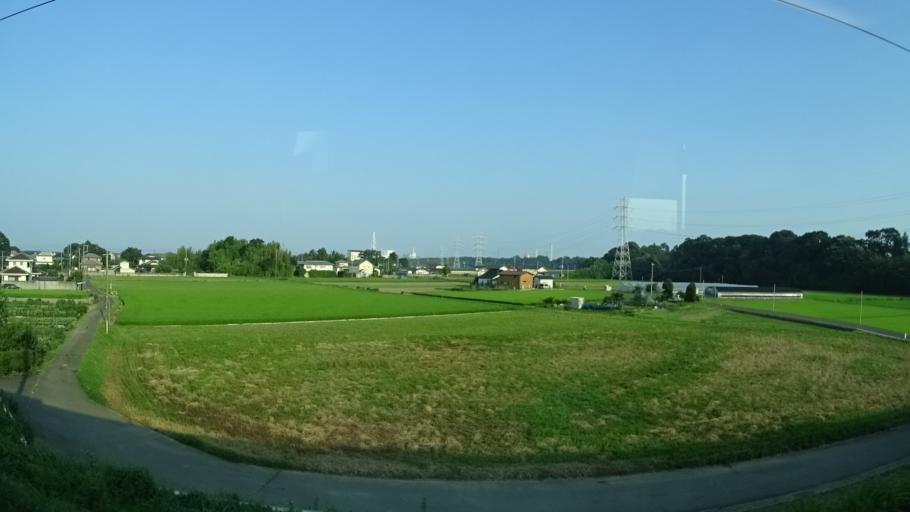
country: JP
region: Ibaraki
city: Funaishikawa
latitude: 36.4812
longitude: 140.5889
